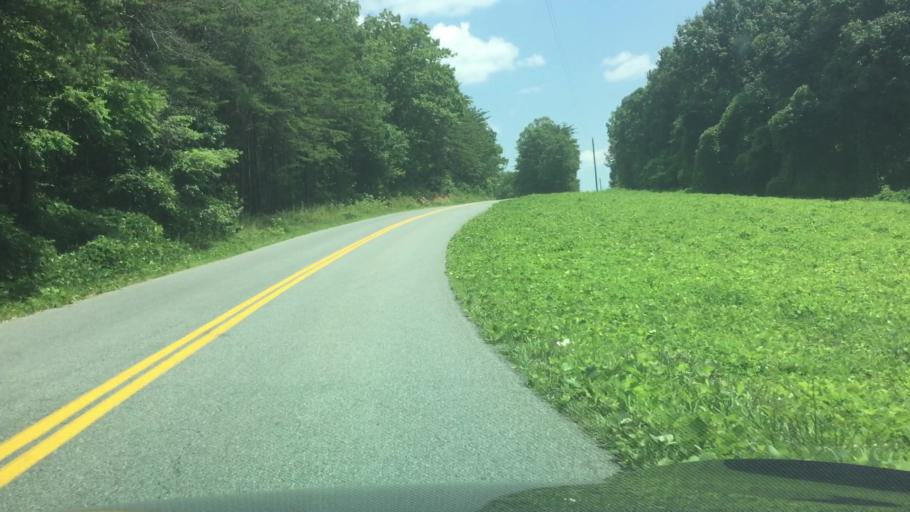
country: US
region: Virginia
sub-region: Appomattox County
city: Appomattox
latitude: 37.3195
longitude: -78.8487
